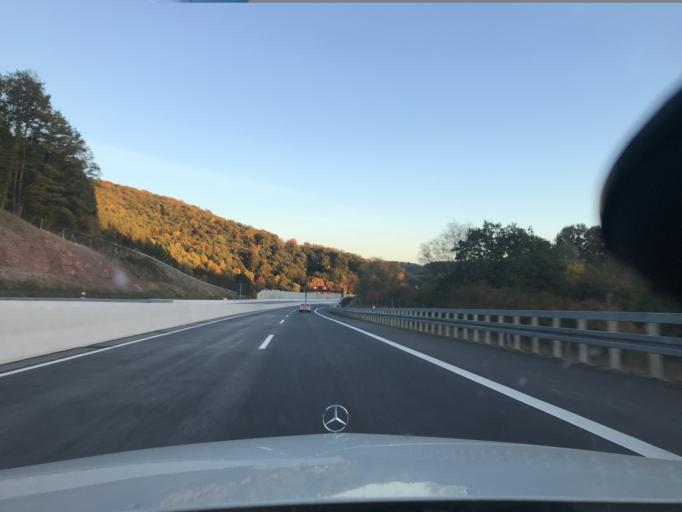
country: DE
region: Hesse
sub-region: Regierungsbezirk Kassel
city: Grossalmerode
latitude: 51.1870
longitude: 9.7963
